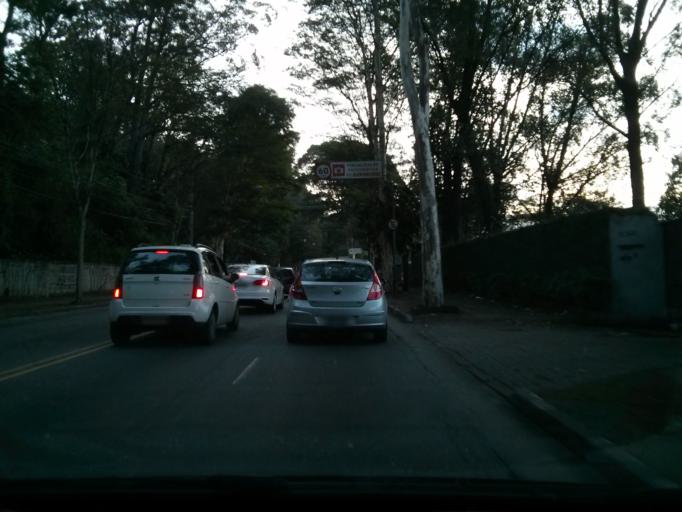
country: BR
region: Sao Paulo
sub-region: Taboao Da Serra
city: Taboao da Serra
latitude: -23.6171
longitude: -46.7084
